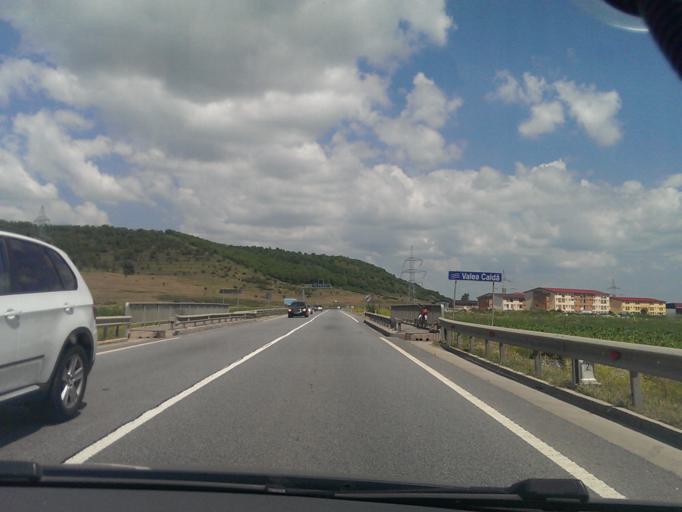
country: RO
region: Cluj
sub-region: Comuna Apahida
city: Apahida
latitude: 46.8105
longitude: 23.7358
